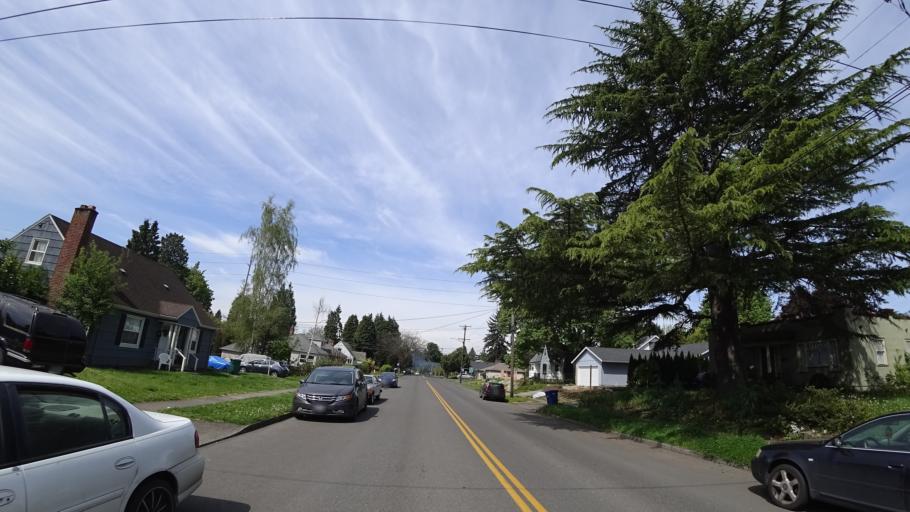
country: US
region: Oregon
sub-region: Clackamas County
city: Milwaukie
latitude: 45.4466
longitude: -122.6211
